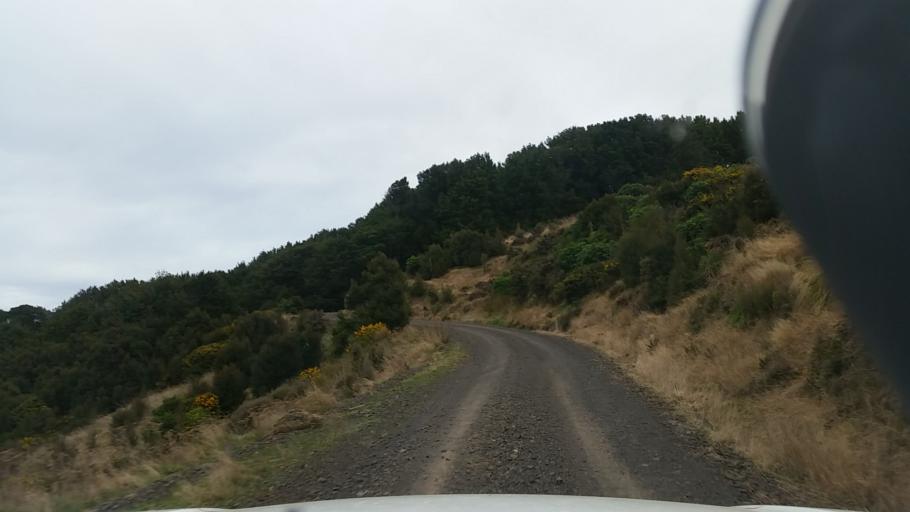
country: NZ
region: Canterbury
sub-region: Christchurch City
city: Christchurch
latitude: -43.8362
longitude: 173.0034
